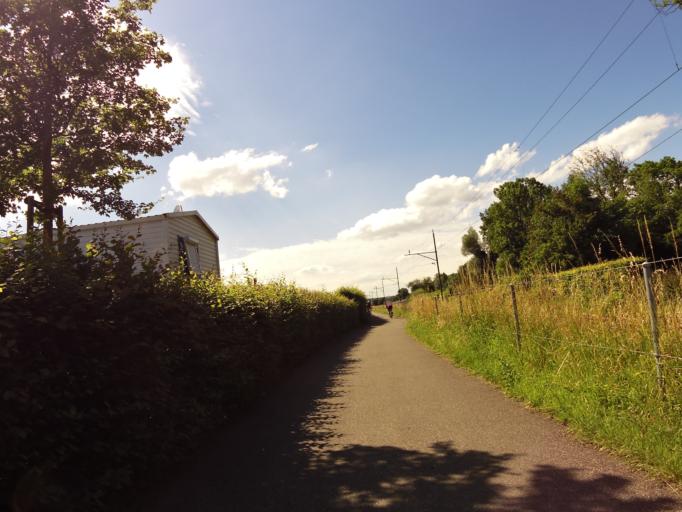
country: CH
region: Thurgau
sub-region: Arbon District
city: Egnach
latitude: 47.5379
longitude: 9.3976
